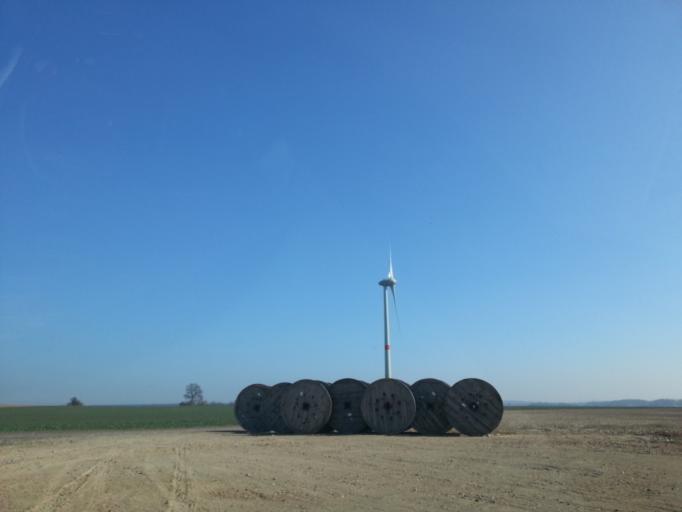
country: DE
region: Saxony
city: Niederschona
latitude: 50.9192
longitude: 13.4099
